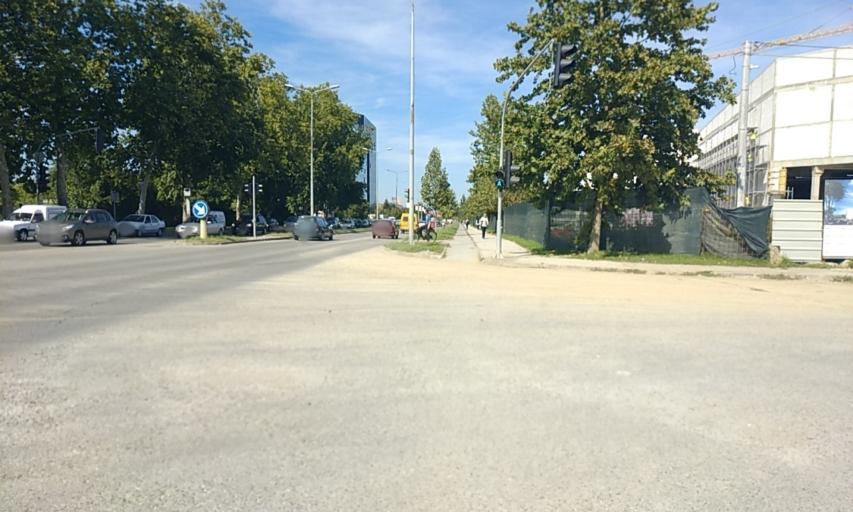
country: BA
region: Republika Srpska
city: Banja Luka
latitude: 44.7788
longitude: 17.2065
